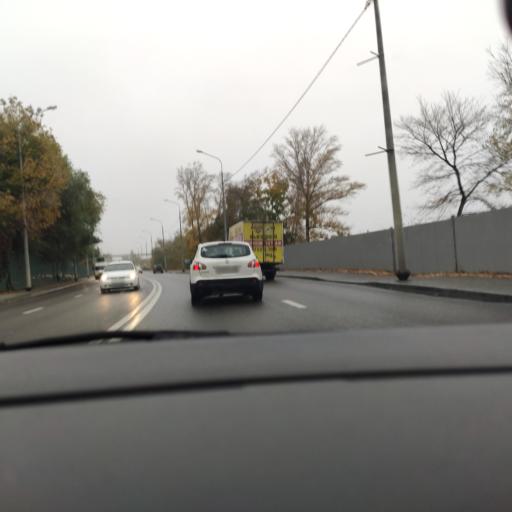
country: RU
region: Voronezj
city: Voronezh
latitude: 51.6876
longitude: 39.2310
